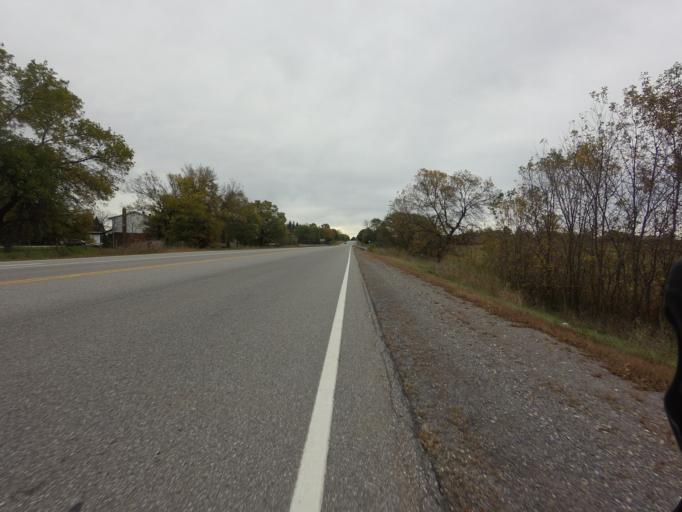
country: CA
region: Ontario
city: Gananoque
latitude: 44.4717
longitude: -76.2417
